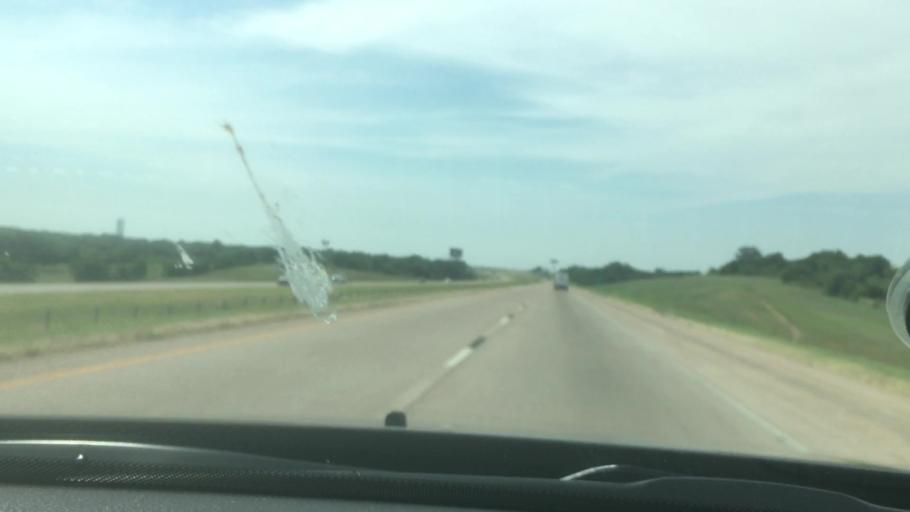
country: US
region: Oklahoma
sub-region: Garvin County
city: Pauls Valley
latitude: 34.7209
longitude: -97.2528
